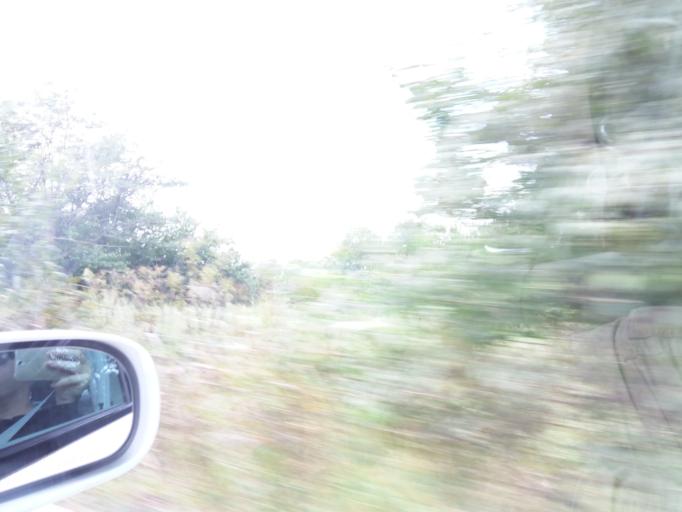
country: US
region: Kentucky
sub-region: Oldham County
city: Pewee Valley
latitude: 38.2549
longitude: -85.4570
